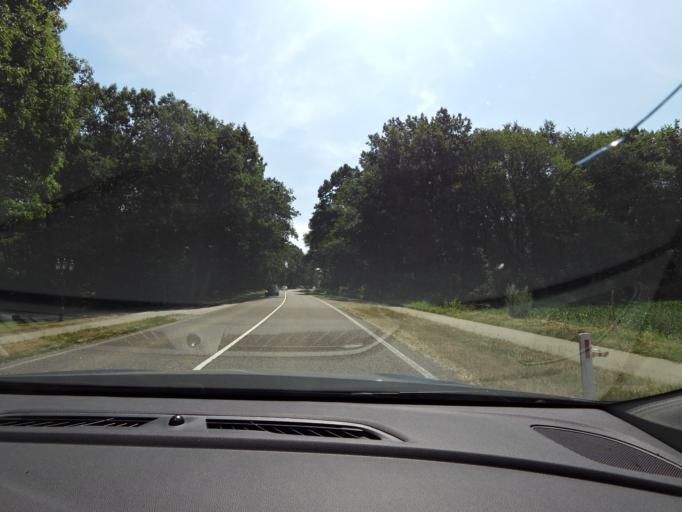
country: NL
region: Limburg
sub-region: Gemeente Leudal
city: Heythuysen
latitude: 51.2250
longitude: 5.9193
